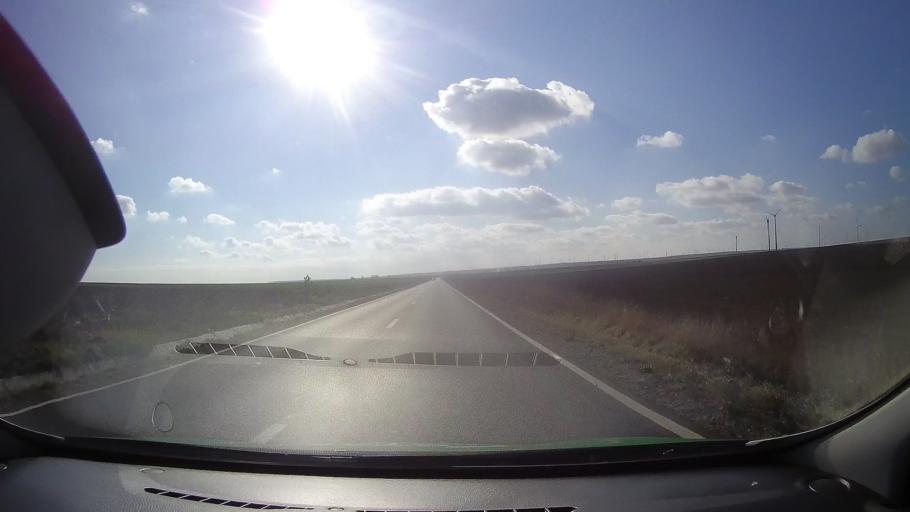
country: RO
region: Constanta
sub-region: Comuna Mihai Viteazu
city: Mihai Viteazu
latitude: 44.6731
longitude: 28.6845
